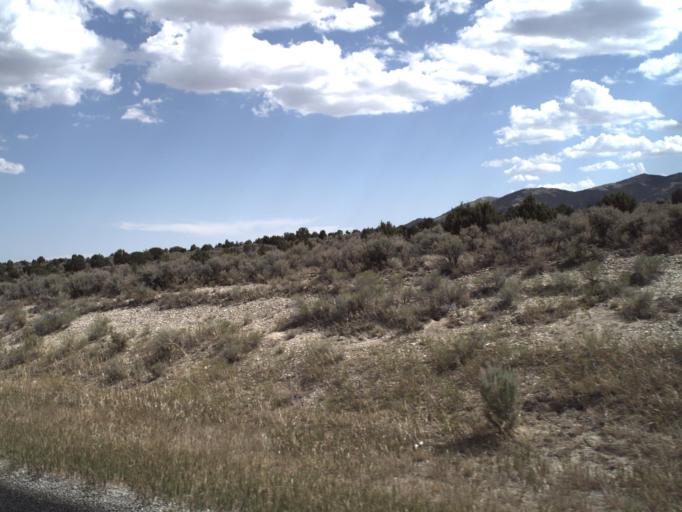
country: US
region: Idaho
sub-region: Minidoka County
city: Rupert
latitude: 41.9858
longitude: -113.1761
